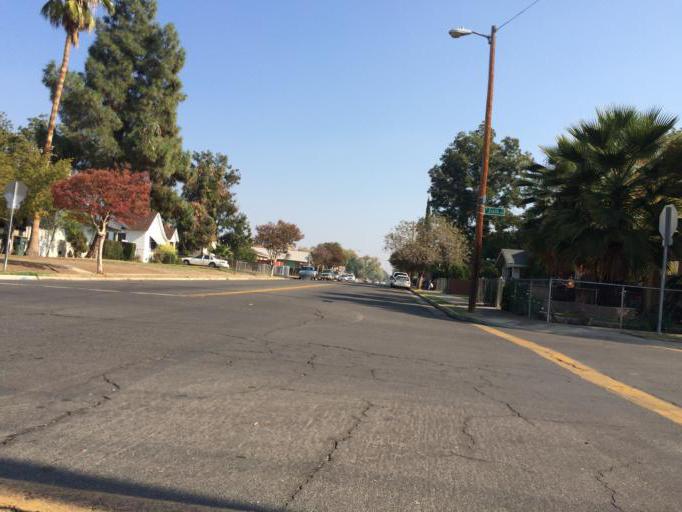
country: US
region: California
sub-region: Fresno County
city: Fresno
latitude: 36.7468
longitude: -119.7645
